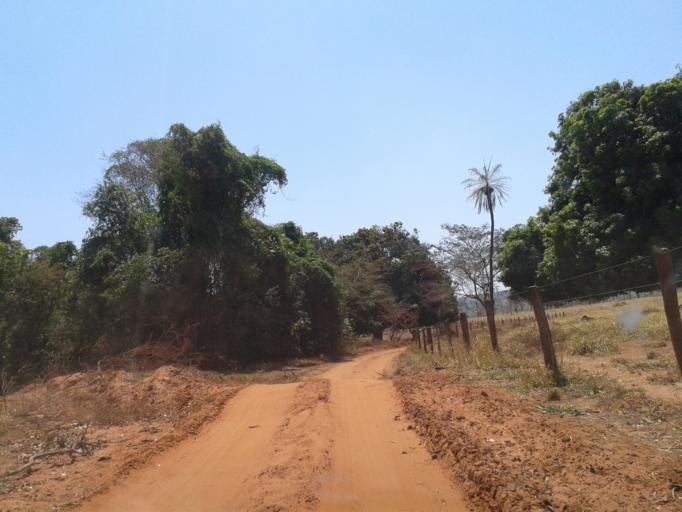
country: BR
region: Minas Gerais
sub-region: Ituiutaba
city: Ituiutaba
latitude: -19.0500
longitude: -49.3776
